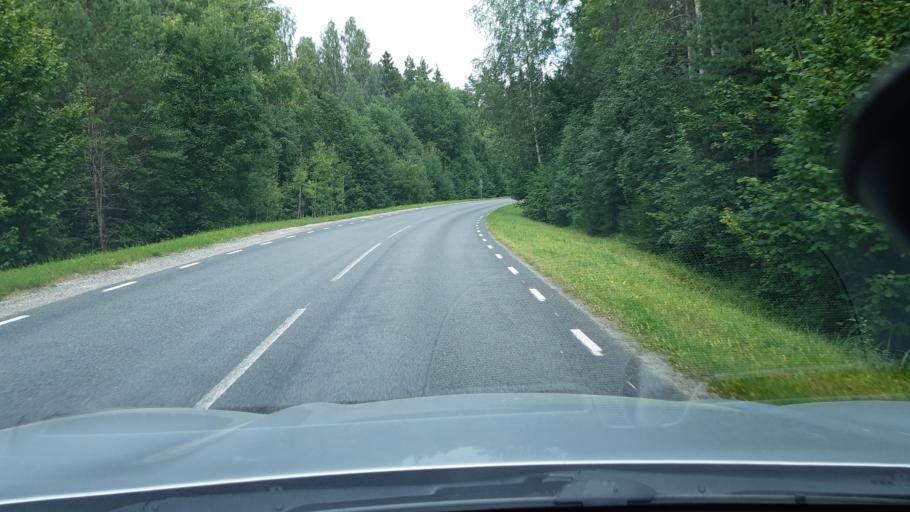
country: EE
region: Raplamaa
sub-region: Maerjamaa vald
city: Marjamaa
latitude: 59.0428
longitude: 24.5117
